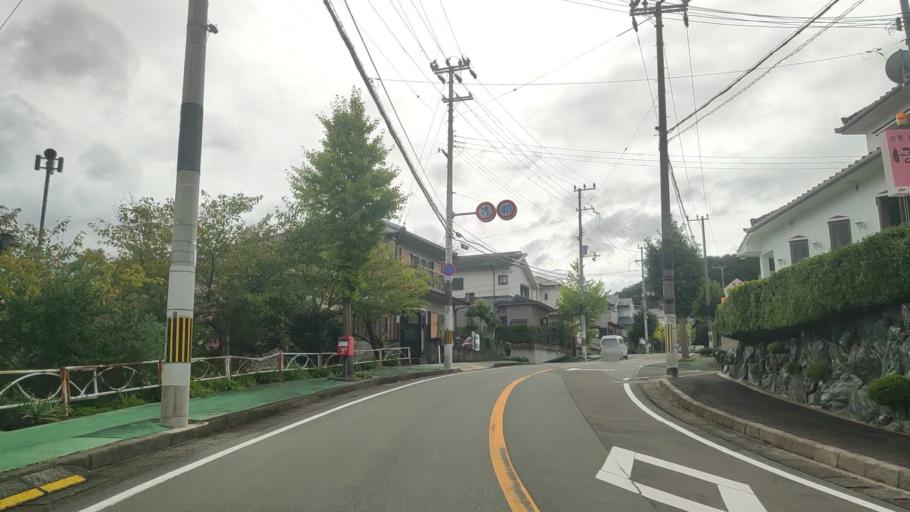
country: JP
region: Wakayama
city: Tanabe
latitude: 33.6762
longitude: 135.3760
